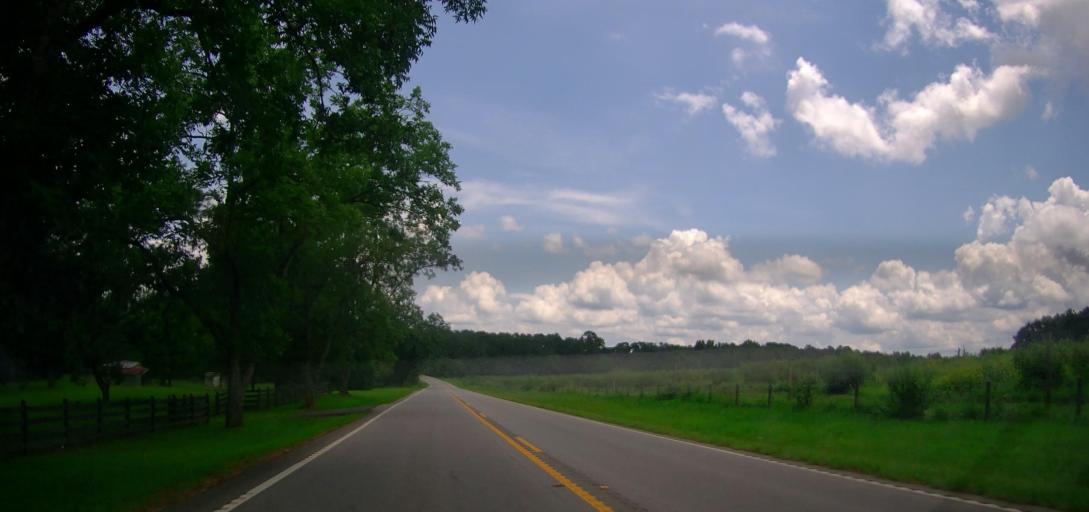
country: US
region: Georgia
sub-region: Meriwether County
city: Greenville
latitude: 32.9856
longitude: -84.6155
